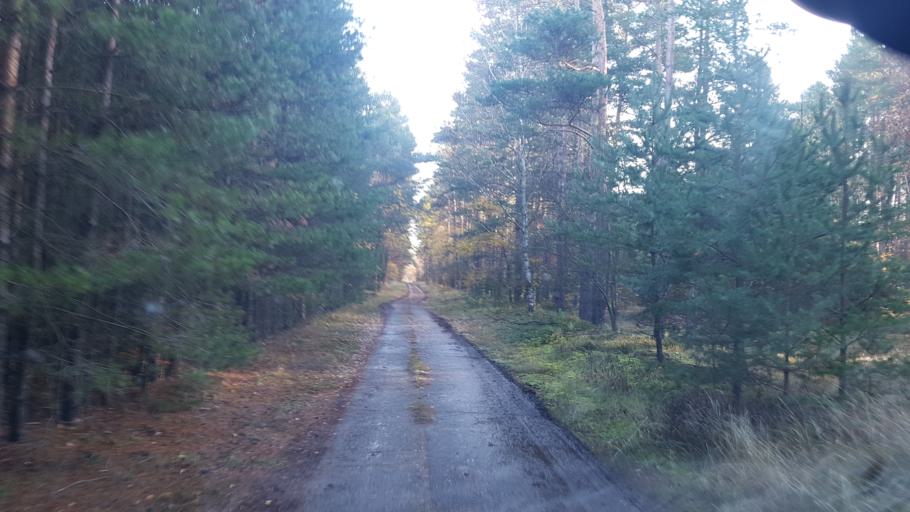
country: DE
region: Brandenburg
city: Crinitz
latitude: 51.7100
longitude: 13.7396
